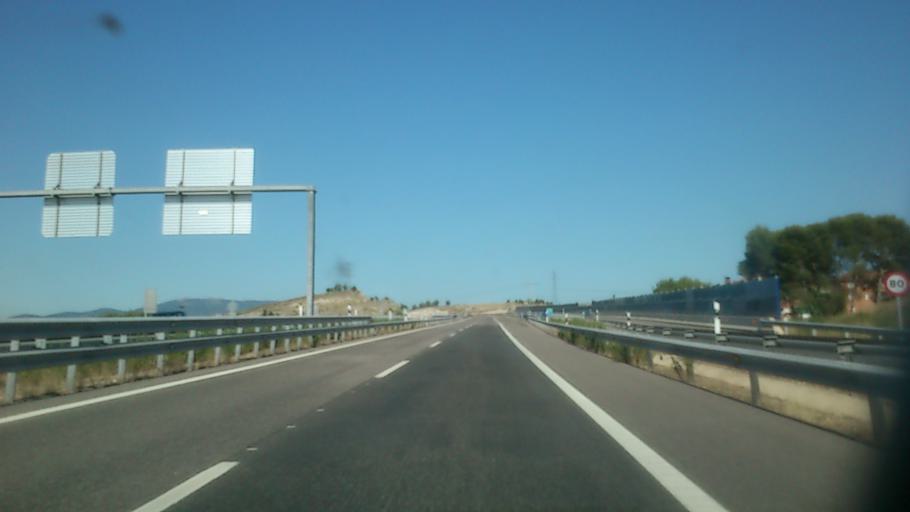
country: ES
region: Aragon
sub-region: Provincia de Zaragoza
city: Calatayud
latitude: 41.3339
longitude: -1.6459
